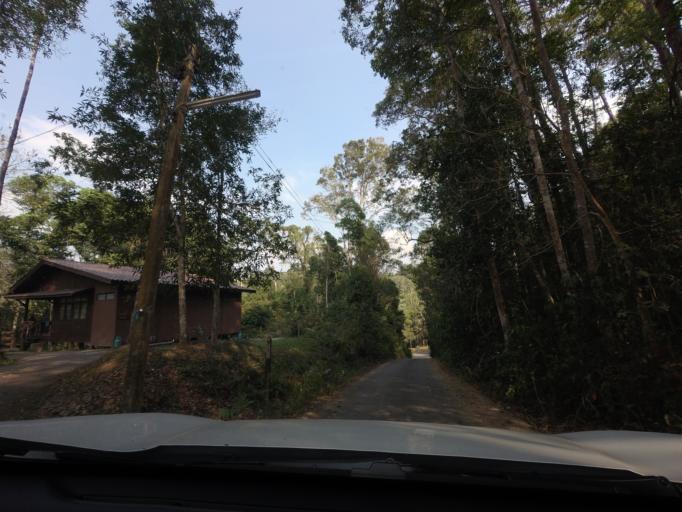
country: TH
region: Nakhon Ratchasima
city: Pak Chong
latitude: 14.4377
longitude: 101.3744
